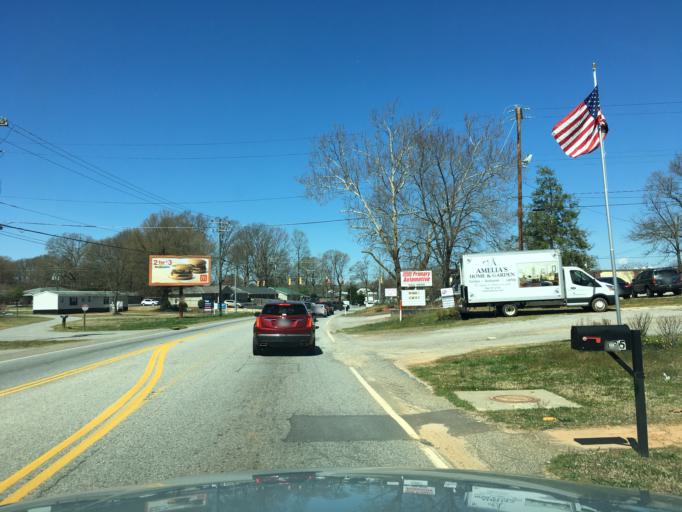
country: US
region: South Carolina
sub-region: Spartanburg County
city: Fairforest
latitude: 34.9319
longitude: -82.0015
